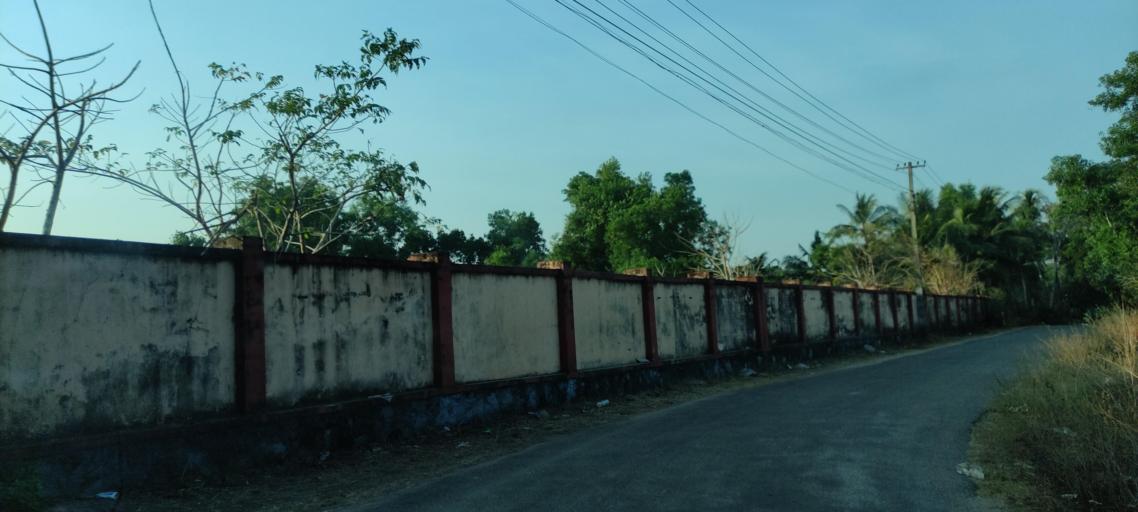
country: IN
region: Kerala
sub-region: Alappuzha
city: Vayalar
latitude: 9.7244
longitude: 76.3568
